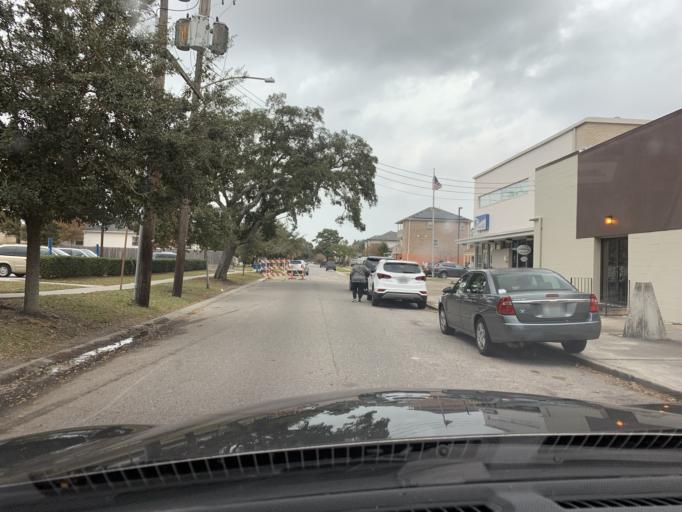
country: US
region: Louisiana
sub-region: Jefferson Parish
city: Metairie
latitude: 30.0047
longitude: -90.1037
